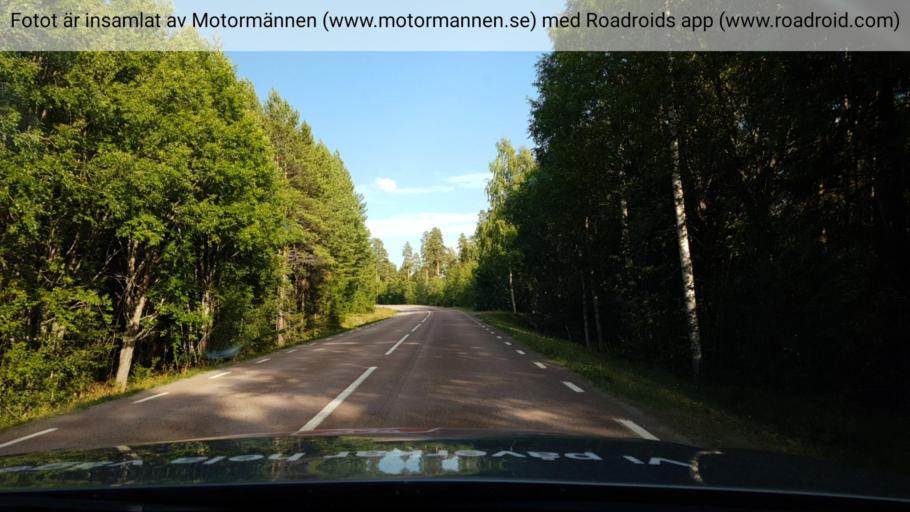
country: SE
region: Vaesternorrland
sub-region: Solleftea Kommun
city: As
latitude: 63.5880
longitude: 16.2955
